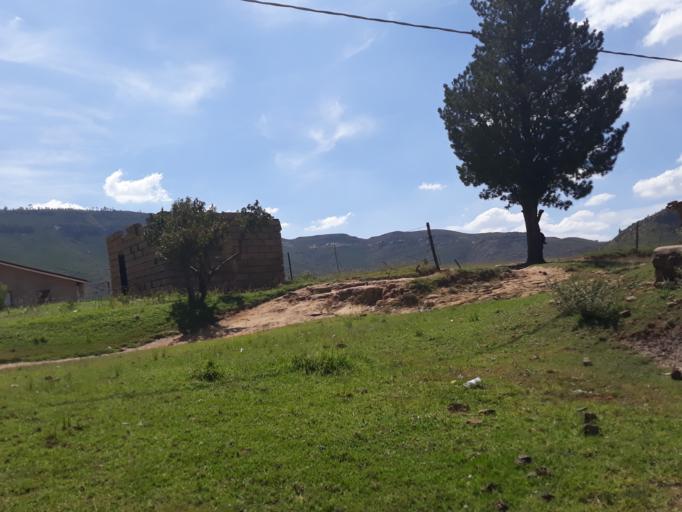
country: LS
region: Mohale's Hoek District
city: Mohale's Hoek
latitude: -30.1025
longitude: 27.4720
